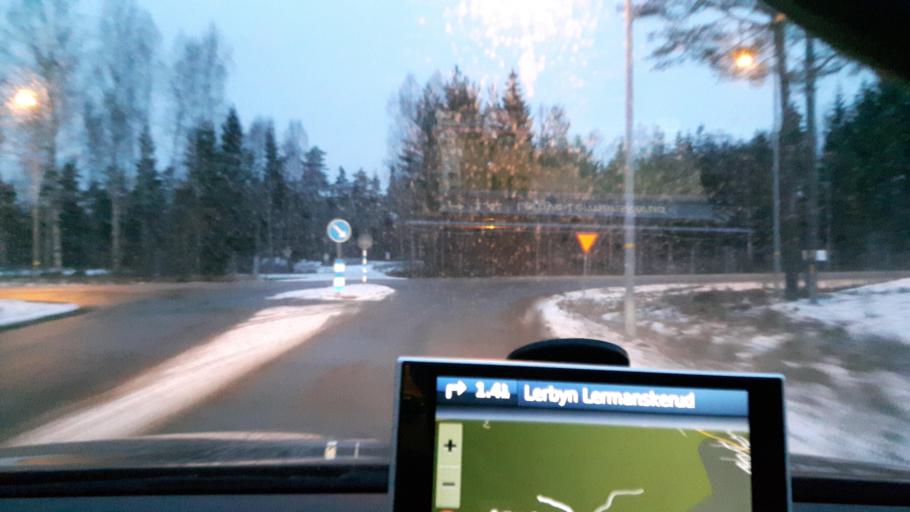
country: SE
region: Vaermland
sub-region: Saffle Kommun
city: Saeffle
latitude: 59.1276
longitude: 12.8822
